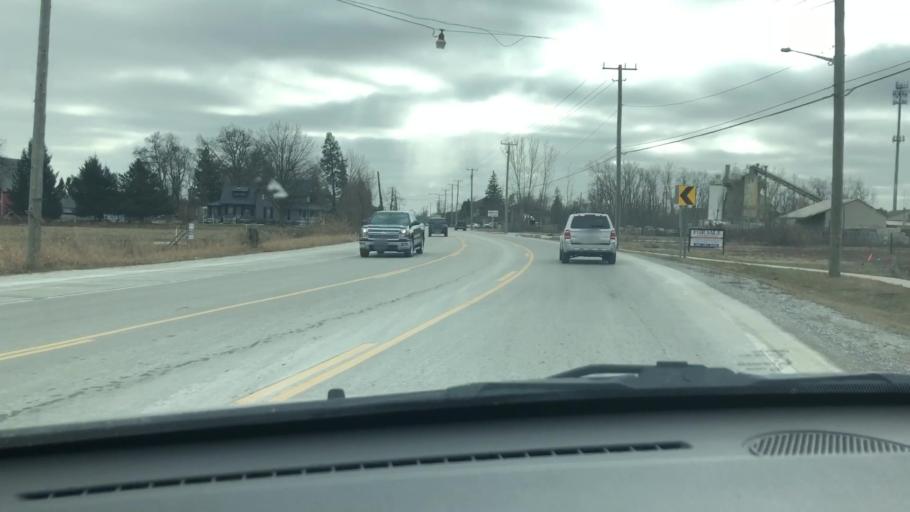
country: US
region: Michigan
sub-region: Macomb County
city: Shelby
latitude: 42.7338
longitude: -83.0362
